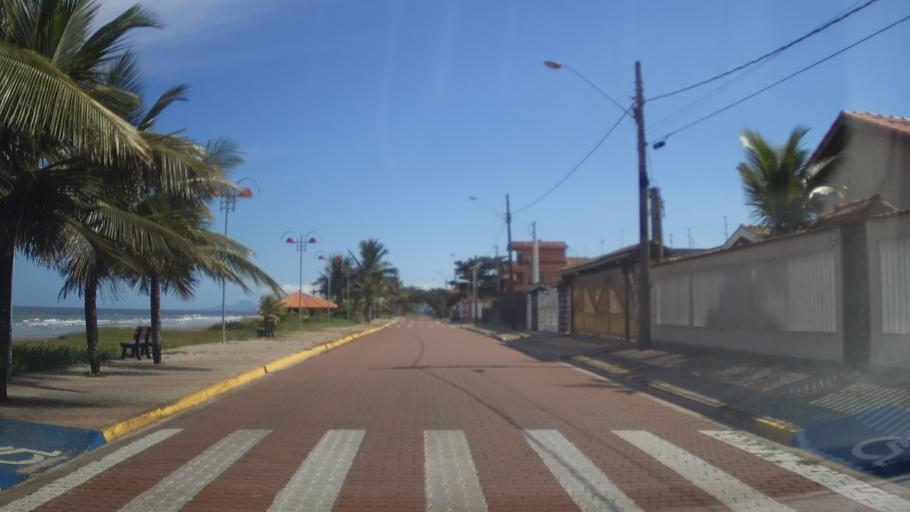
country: BR
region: Sao Paulo
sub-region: Itanhaem
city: Itanhaem
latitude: -24.1700
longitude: -46.7575
